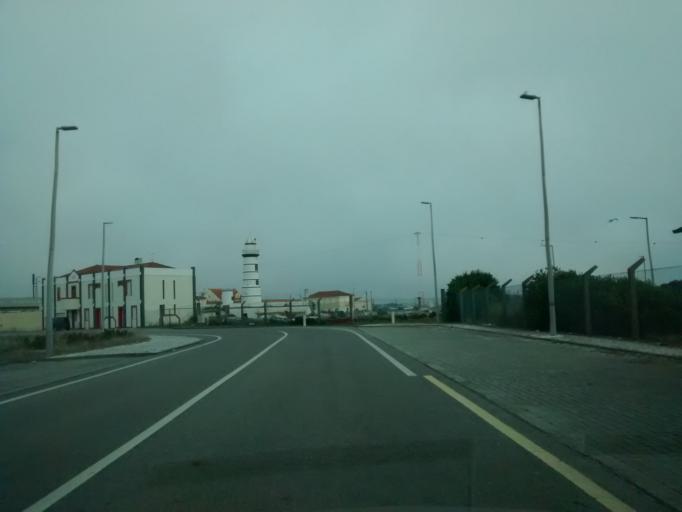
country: PT
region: Aveiro
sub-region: Ilhavo
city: Gafanha da Nazare
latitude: 40.6463
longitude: -8.7338
